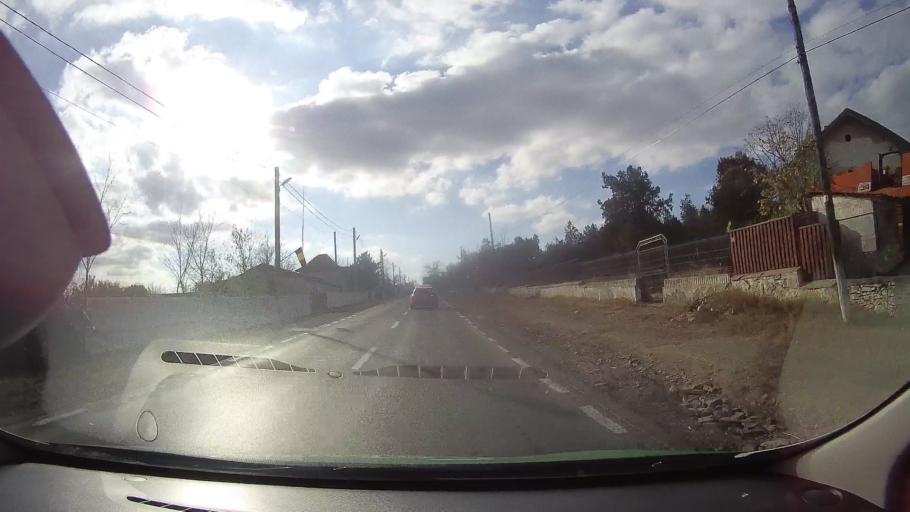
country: RO
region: Tulcea
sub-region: Comuna Topolog
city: Topolog
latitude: 44.8726
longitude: 28.3705
